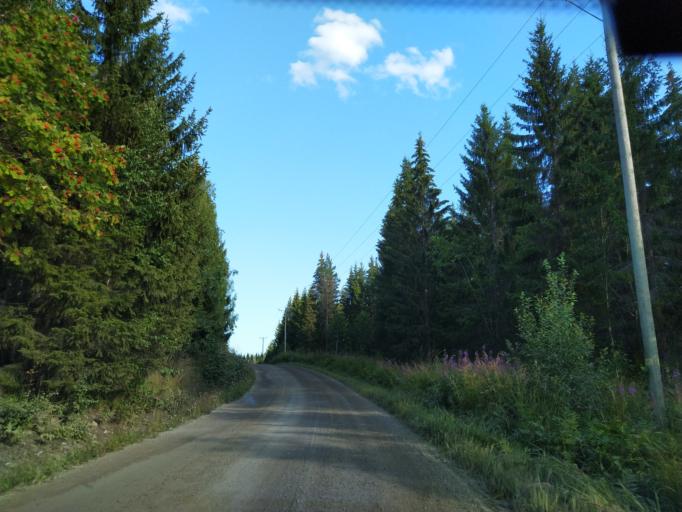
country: FI
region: Central Finland
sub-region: Jaemsae
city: Kuhmoinen
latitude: 61.6928
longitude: 24.9486
